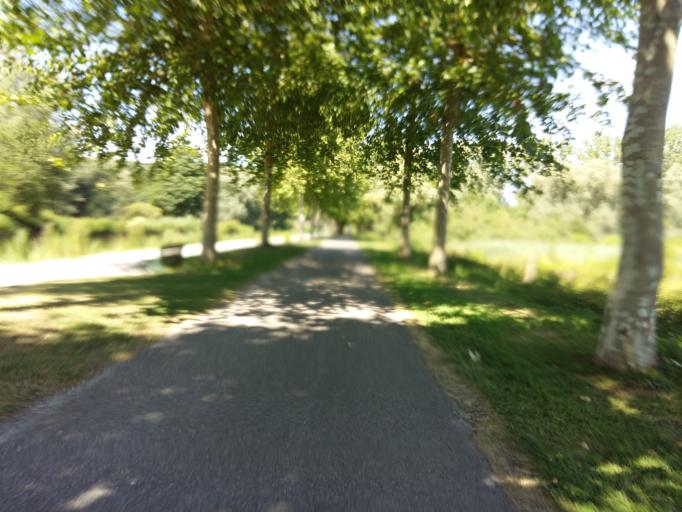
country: FR
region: Picardie
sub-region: Departement de la Somme
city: Amiens
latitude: 49.9150
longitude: 2.2700
